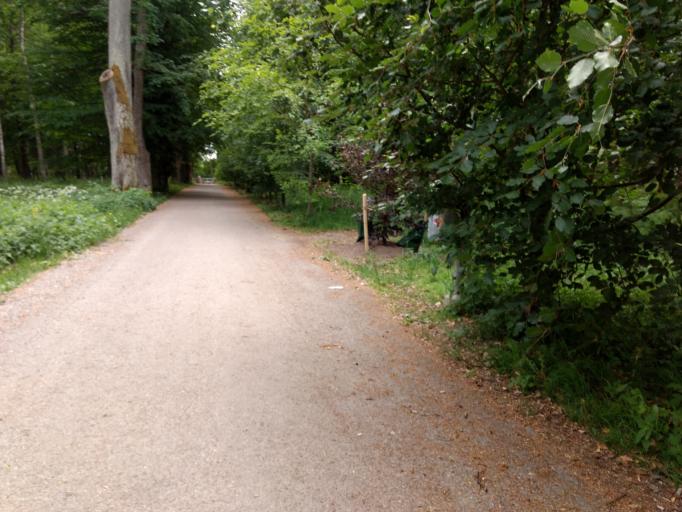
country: SE
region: Stockholm
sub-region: Upplands Vasby Kommun
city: Upplands Vaesby
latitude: 59.5277
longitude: 17.9106
